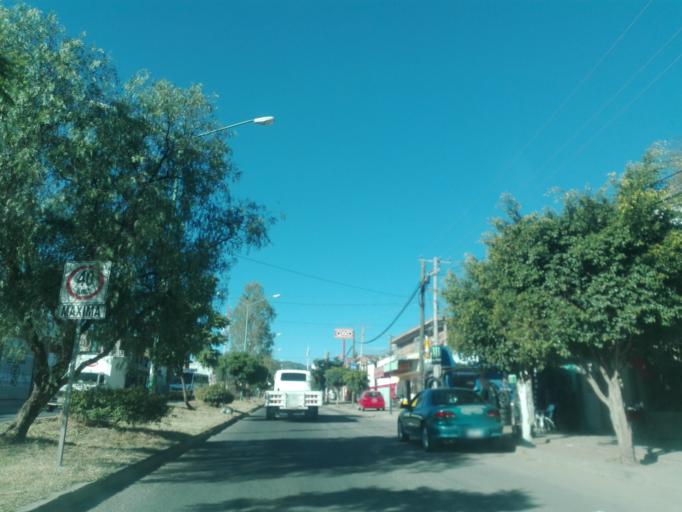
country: MX
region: Guanajuato
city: Leon
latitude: 21.1763
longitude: -101.6757
